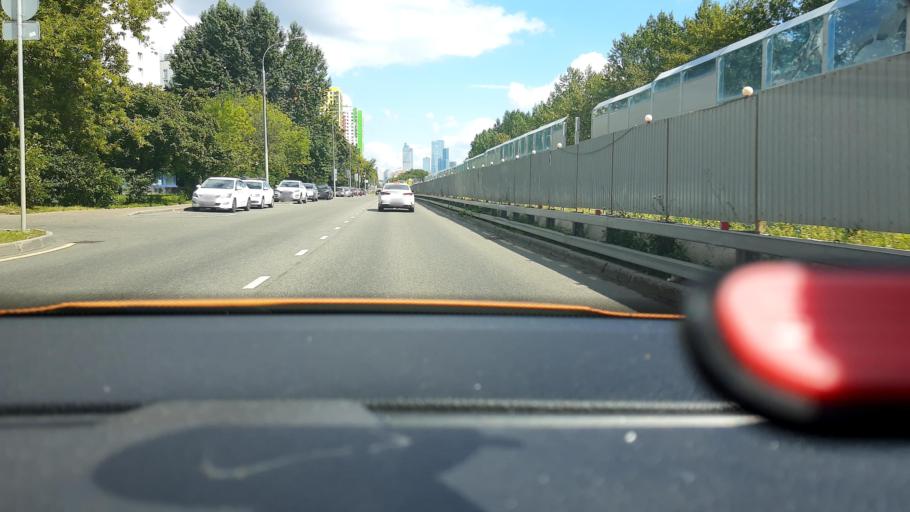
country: RU
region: Moscow
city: Davydkovo
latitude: 55.7339
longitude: 37.4580
